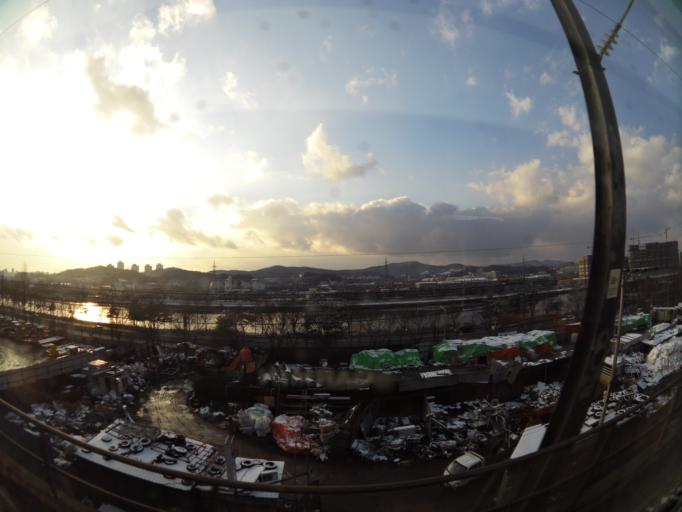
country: KR
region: Daejeon
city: Songgang-dong
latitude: 36.3872
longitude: 127.4136
